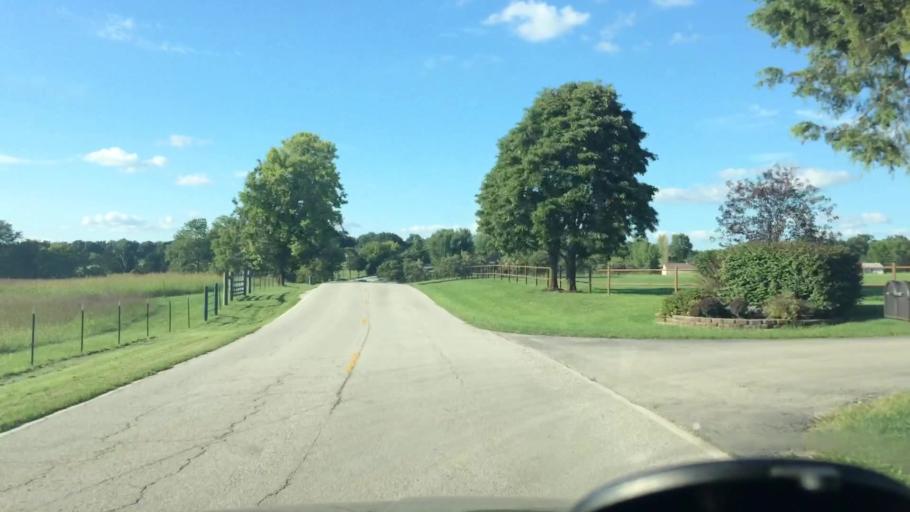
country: US
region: Missouri
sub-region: Greene County
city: Strafford
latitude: 37.2758
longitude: -93.0806
